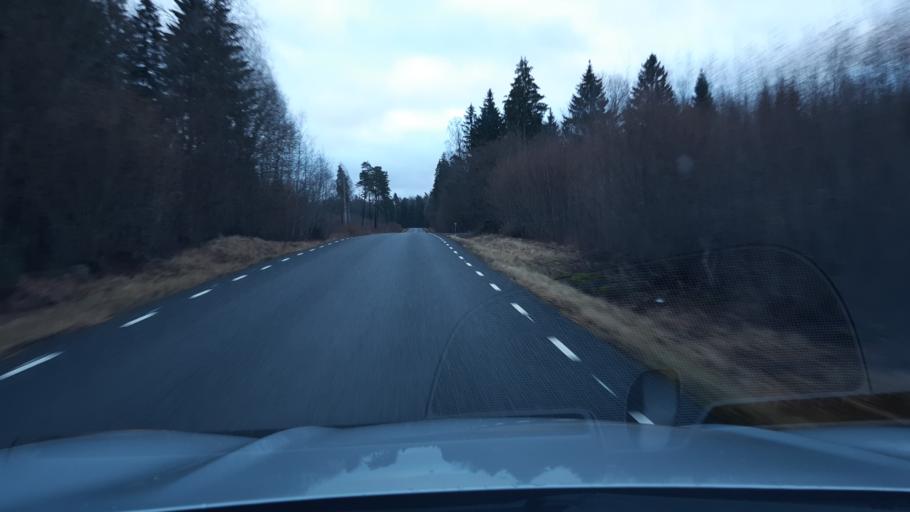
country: EE
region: Harju
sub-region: Saku vald
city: Saku
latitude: 59.1826
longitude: 24.6098
